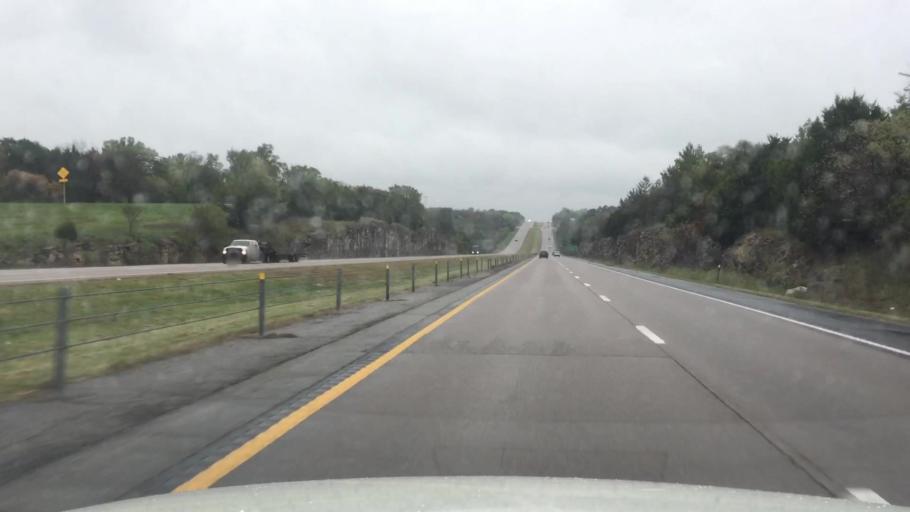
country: US
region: Missouri
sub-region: Boone County
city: Ashland
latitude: 38.7081
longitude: -92.2547
